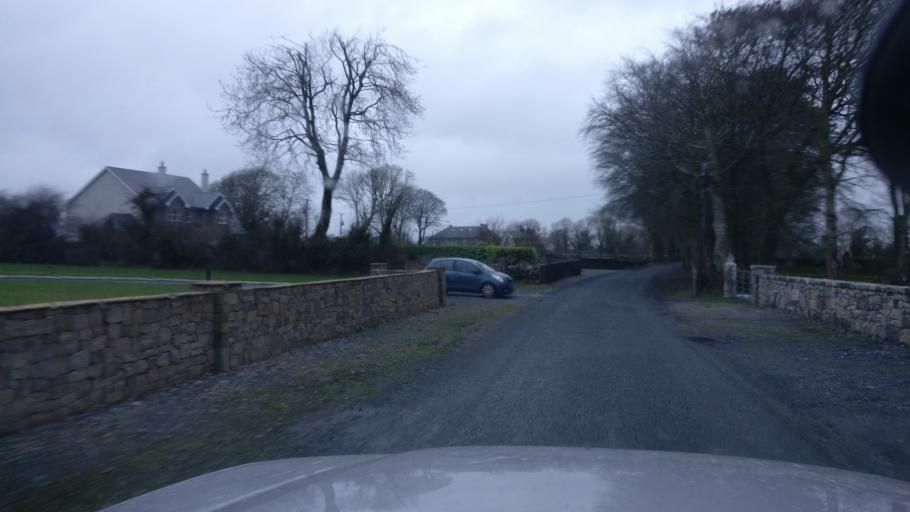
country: IE
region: Connaught
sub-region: County Galway
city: Loughrea
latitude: 53.2115
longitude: -8.6313
